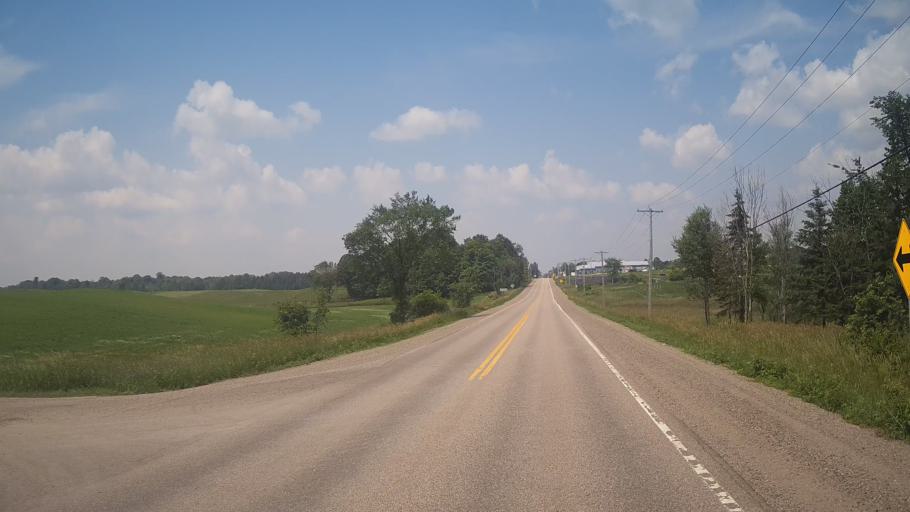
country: CA
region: Quebec
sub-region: Outaouais
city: Shawville
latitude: 45.5943
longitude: -76.4794
